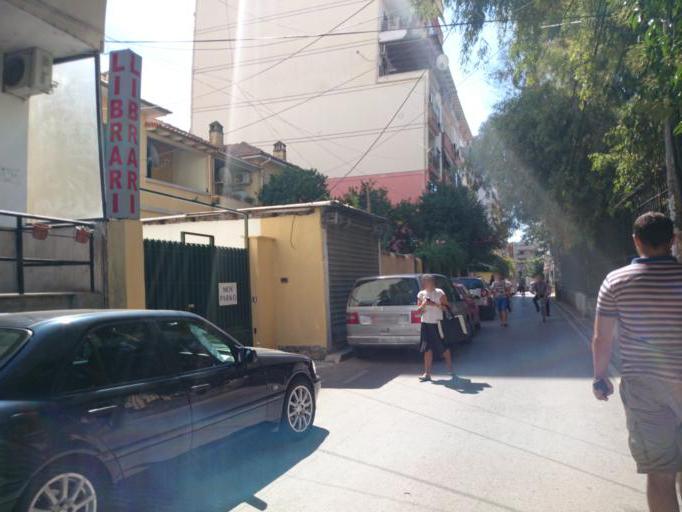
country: AL
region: Tirane
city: Tirana
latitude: 41.3266
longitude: 19.8117
